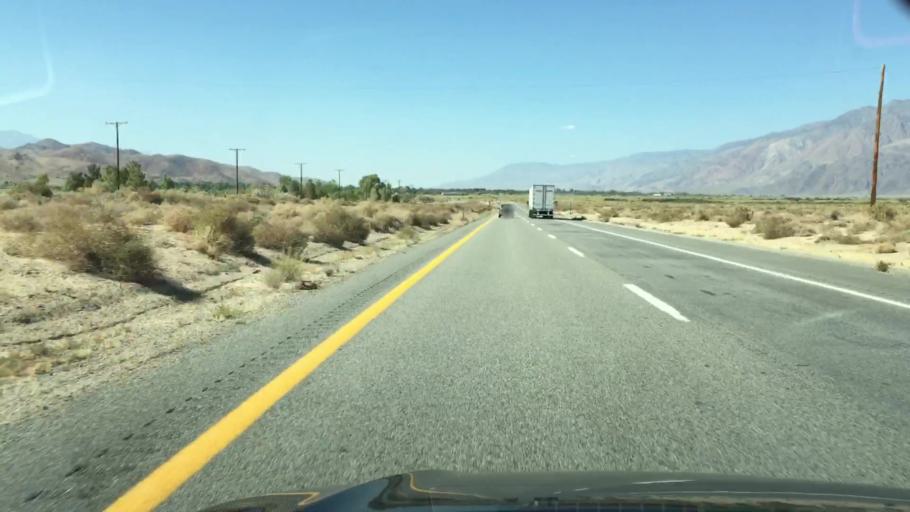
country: US
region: California
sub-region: Inyo County
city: Lone Pine
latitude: 36.5562
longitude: -118.0497
